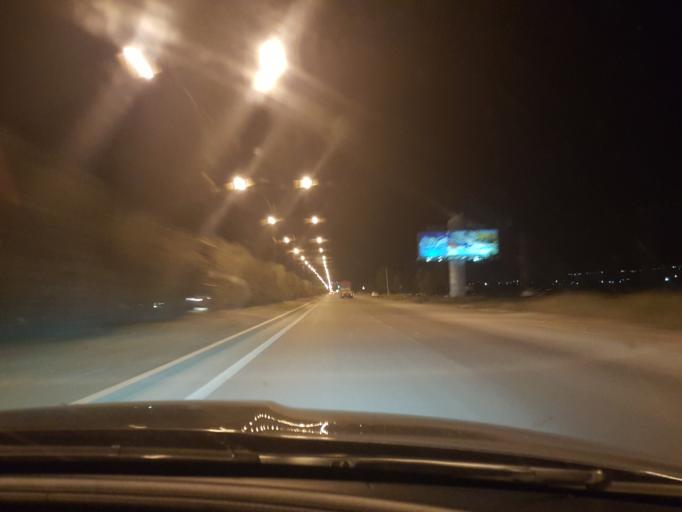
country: IQ
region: Arbil
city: Erbil
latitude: 36.2684
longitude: 44.0949
